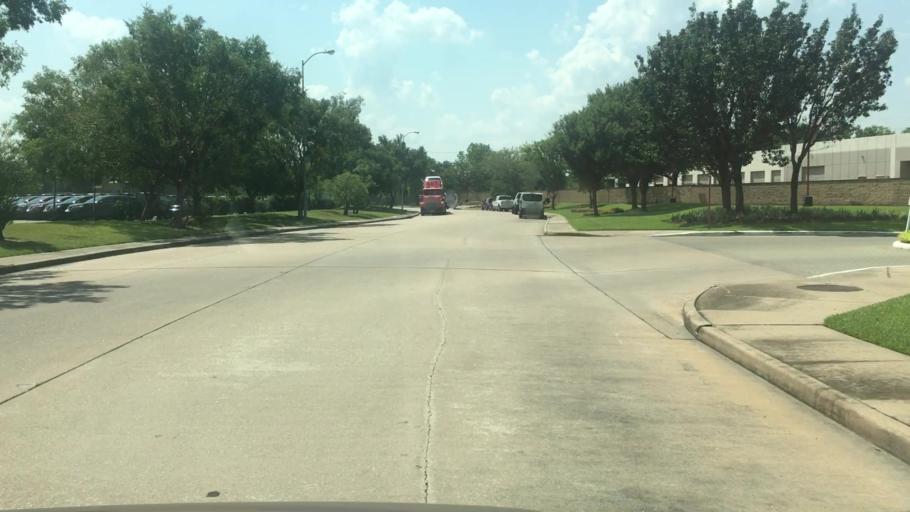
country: US
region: Texas
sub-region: Fort Bend County
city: Meadows Place
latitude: 29.6461
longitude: -95.5703
